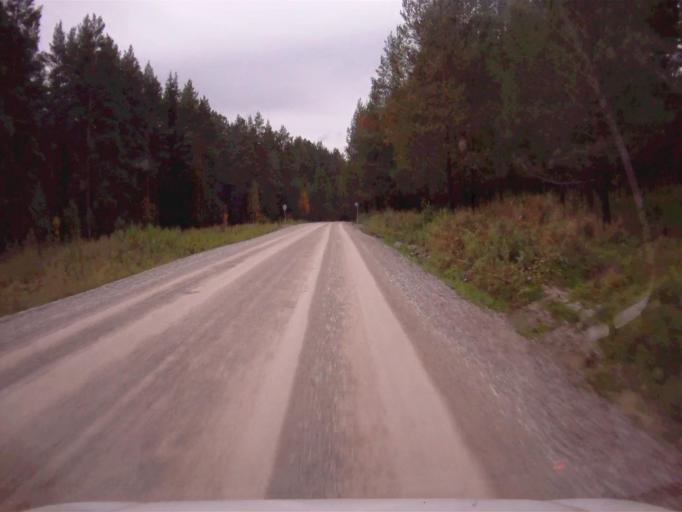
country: RU
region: Chelyabinsk
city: Nyazepetrovsk
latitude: 56.0456
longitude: 59.5199
